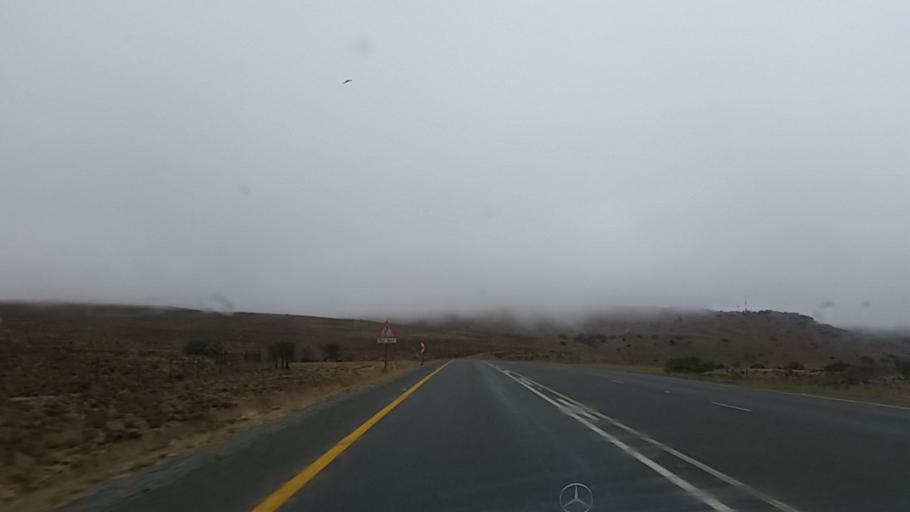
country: ZA
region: Eastern Cape
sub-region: Cacadu District Municipality
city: Graaff-Reinet
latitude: -31.9551
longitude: 24.7271
